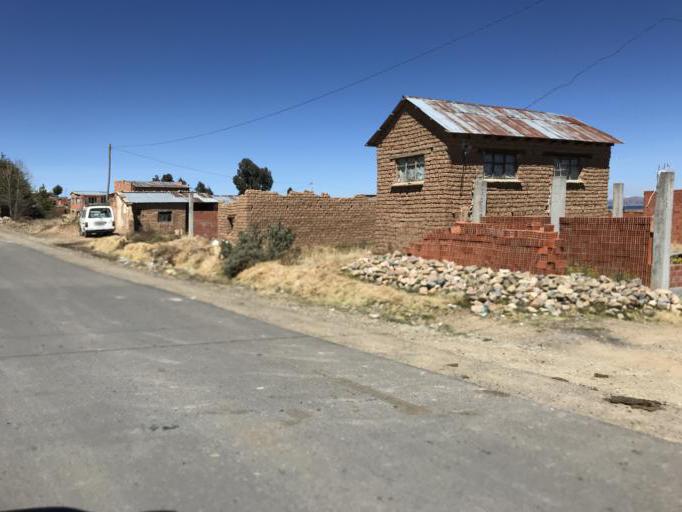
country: BO
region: La Paz
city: Huatajata
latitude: -16.1929
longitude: -68.7313
